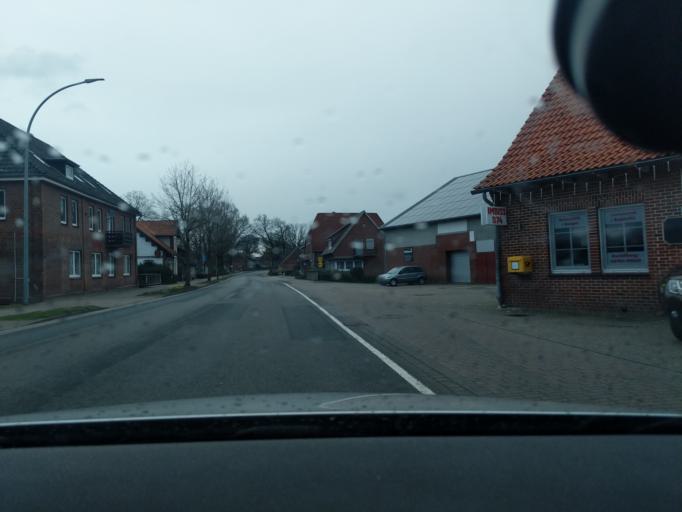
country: DE
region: Lower Saxony
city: Estorf
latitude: 53.5180
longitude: 9.2054
